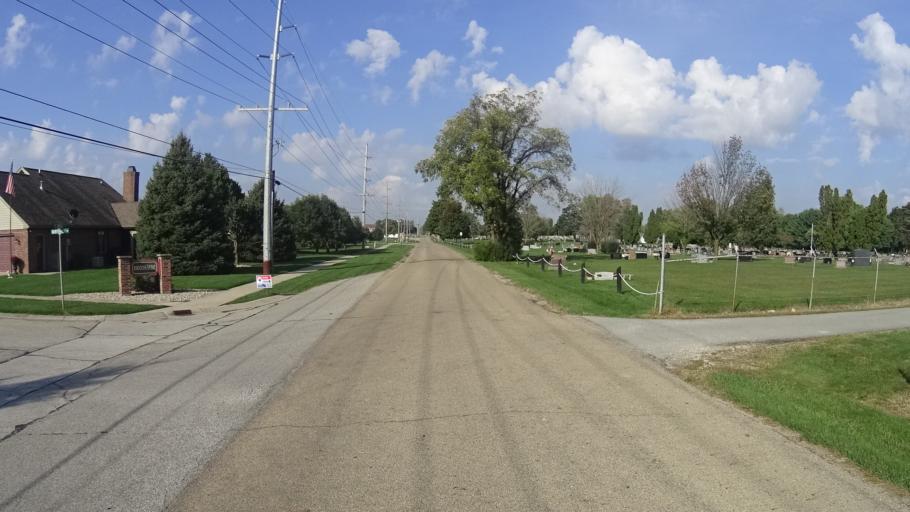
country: US
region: Indiana
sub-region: Madison County
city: Lapel
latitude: 40.0601
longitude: -85.8486
